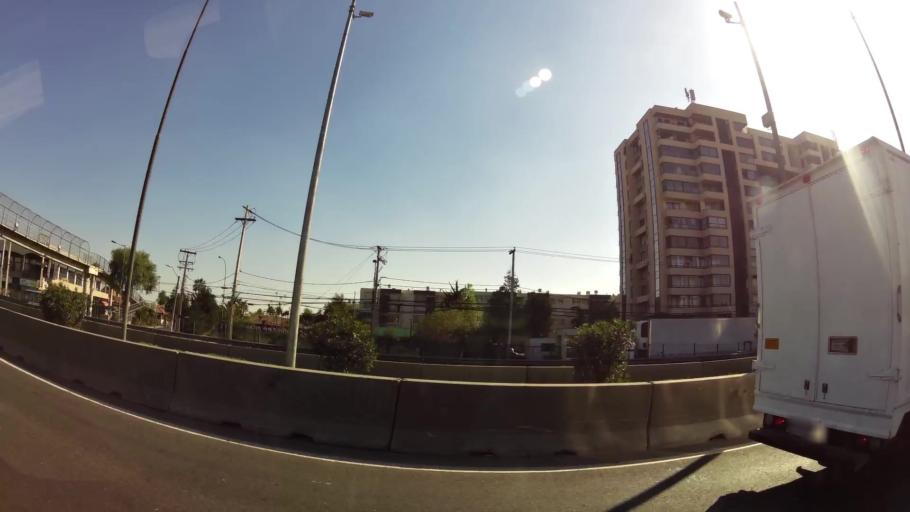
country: CL
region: Santiago Metropolitan
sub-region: Provincia de Santiago
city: Lo Prado
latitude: -33.4829
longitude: -70.7535
